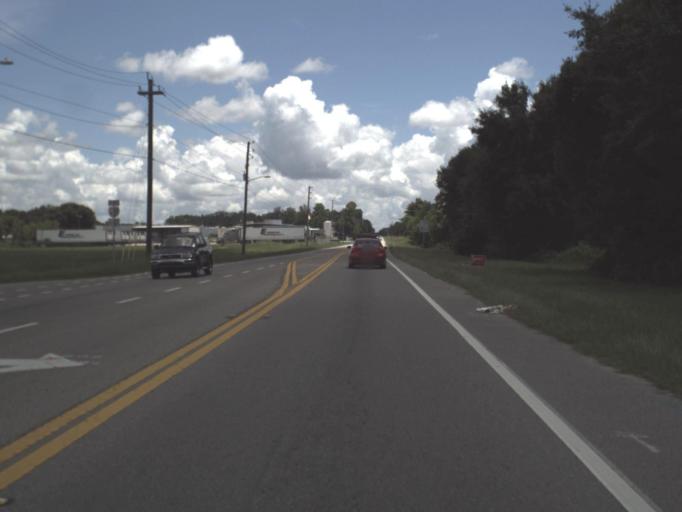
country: US
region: Florida
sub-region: Hillsborough County
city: Dover
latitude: 27.9897
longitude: -82.2436
